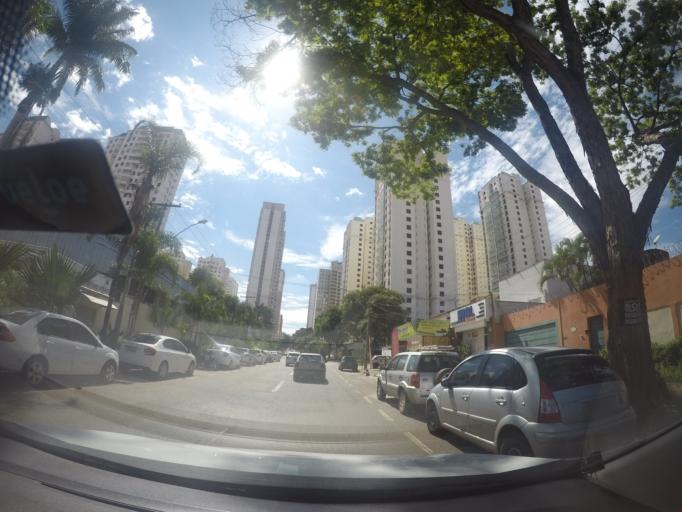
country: BR
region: Goias
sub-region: Goiania
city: Goiania
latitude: -16.7193
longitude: -49.2696
